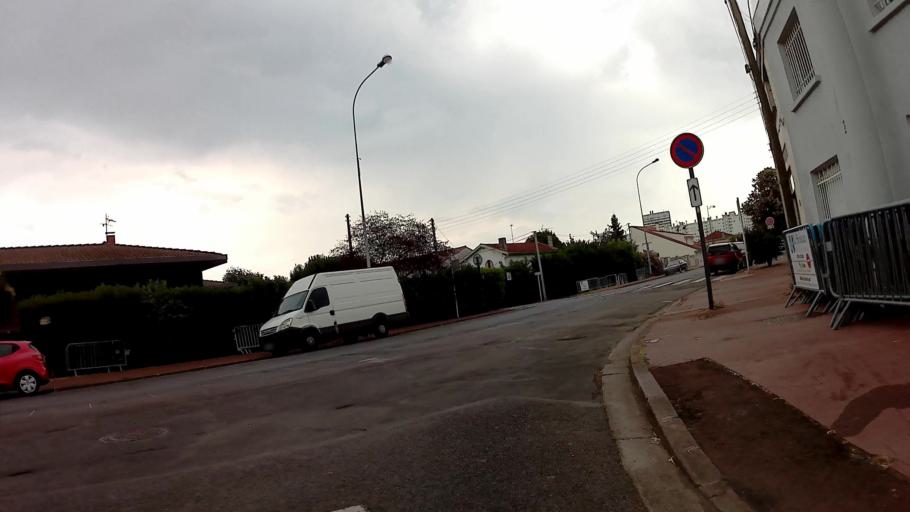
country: FR
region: Aquitaine
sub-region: Departement de la Gironde
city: Le Bouscat
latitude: 44.8653
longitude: -0.5890
